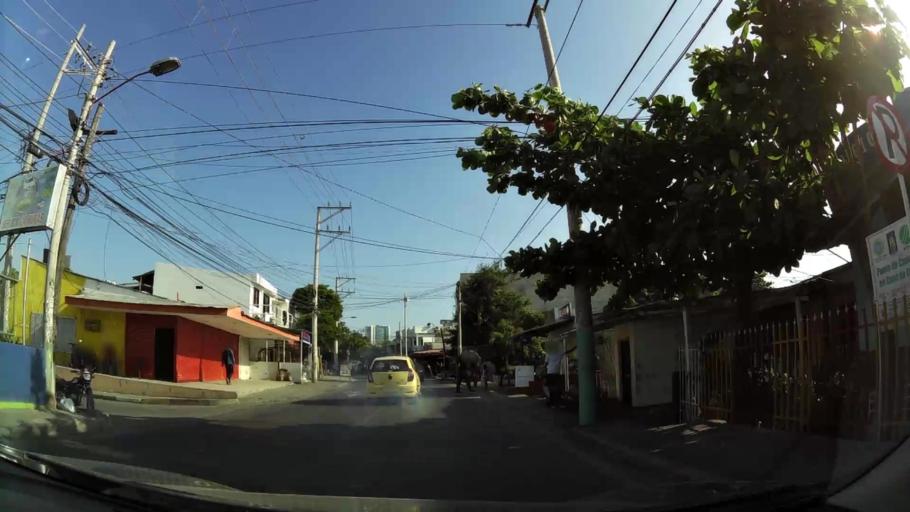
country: CO
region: Bolivar
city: Cartagena
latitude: 10.4036
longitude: -75.4836
